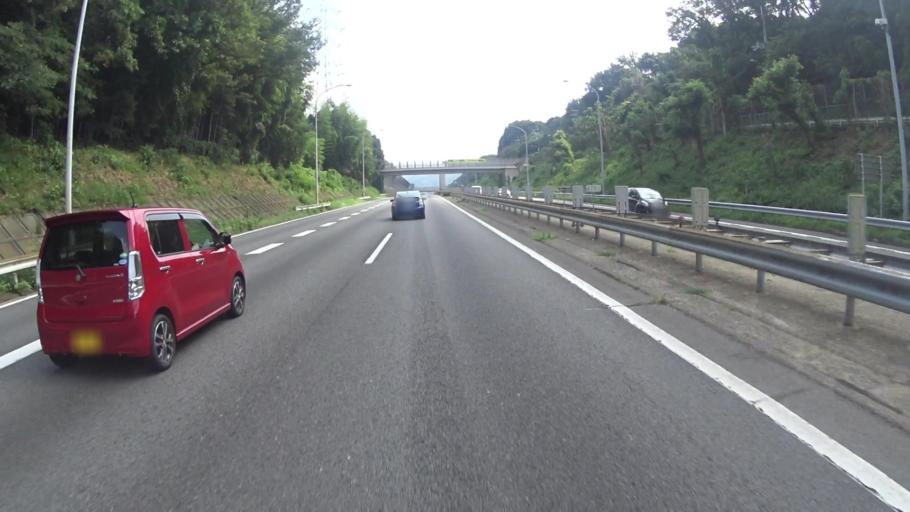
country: JP
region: Shiga Prefecture
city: Otsu-shi
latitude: 34.9757
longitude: 135.8280
